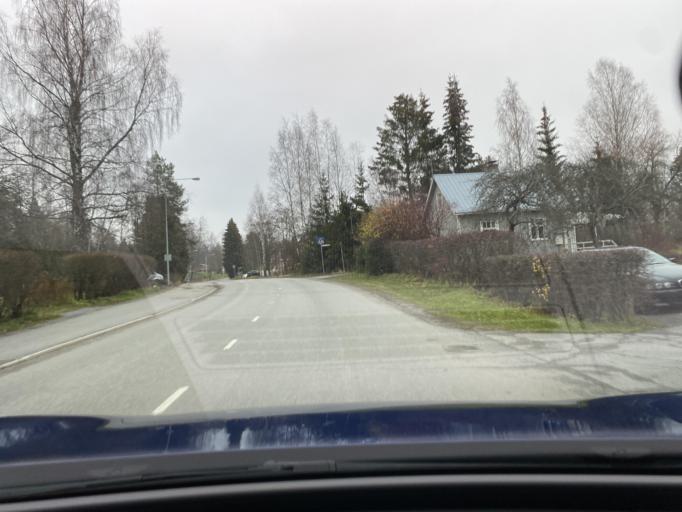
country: FI
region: Pirkanmaa
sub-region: Tampere
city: Nokia
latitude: 61.4575
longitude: 23.4867
